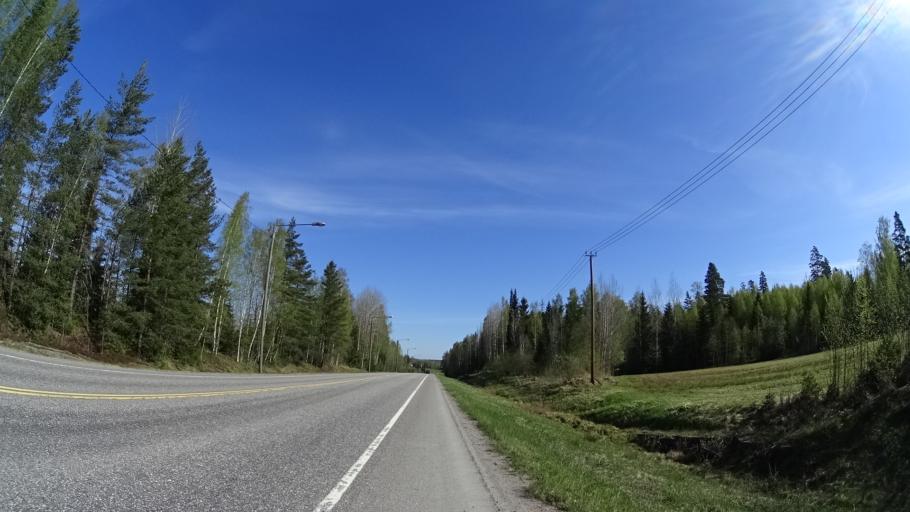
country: FI
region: Uusimaa
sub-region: Helsinki
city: Nurmijaervi
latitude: 60.3843
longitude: 24.8077
